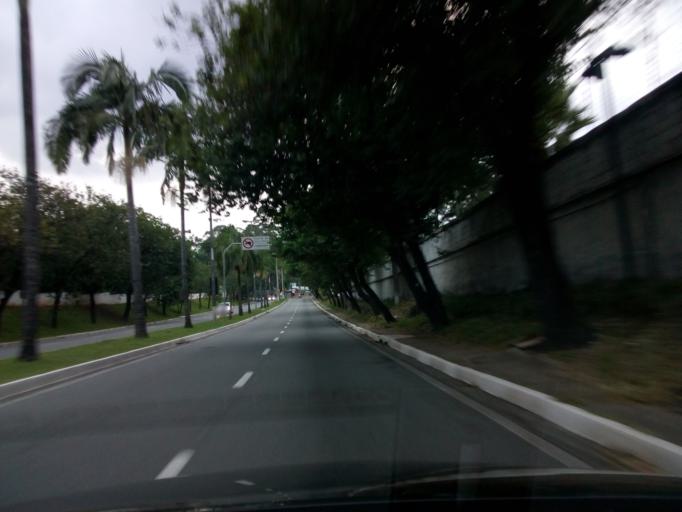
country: BR
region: Sao Paulo
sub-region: Carapicuiba
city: Carapicuiba
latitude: -23.4893
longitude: -46.8395
